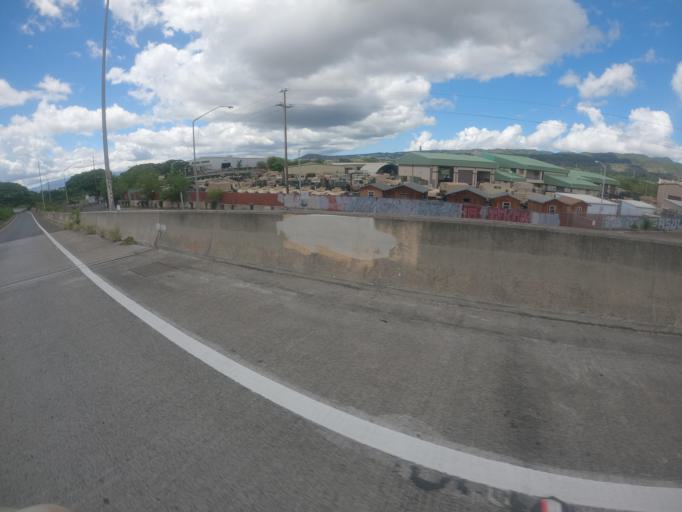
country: US
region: Hawaii
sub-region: Honolulu County
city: Honolulu
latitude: 21.3348
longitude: -157.8912
